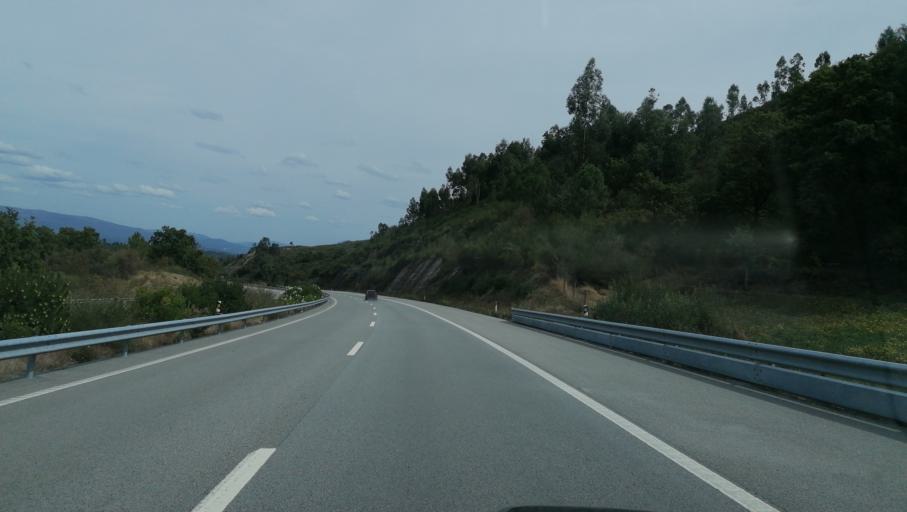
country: PT
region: Braga
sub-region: Celorico de Basto
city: Celorico de Basto
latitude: 41.4469
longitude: -8.0563
